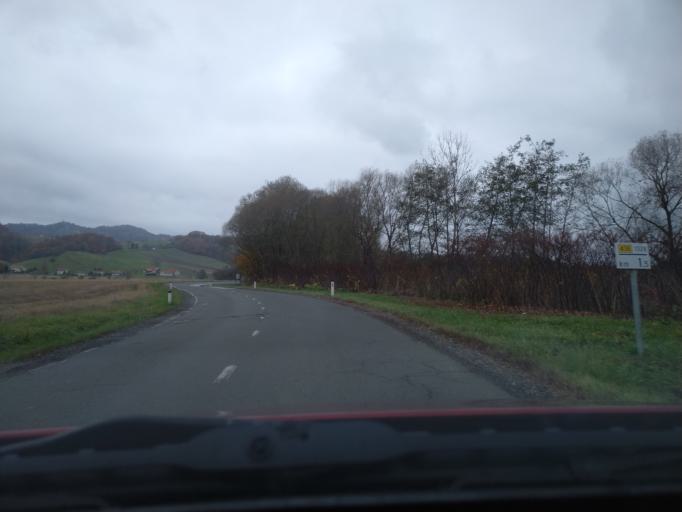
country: SI
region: Pesnica
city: Pesnica pri Mariboru
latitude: 46.6019
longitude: 15.6525
